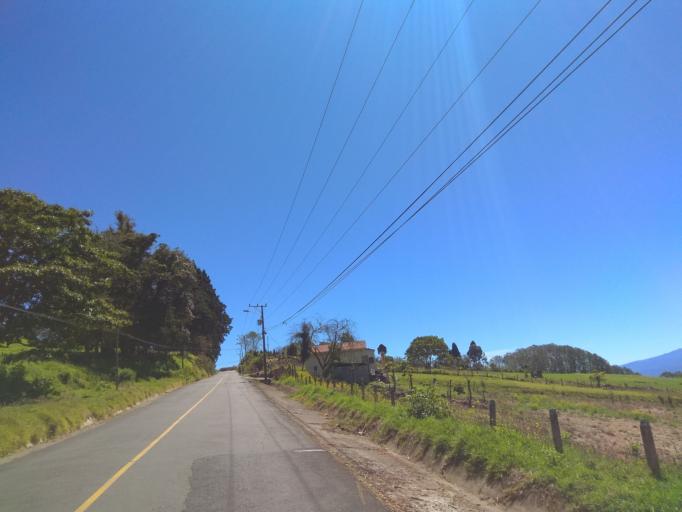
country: CR
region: Cartago
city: Tres Rios
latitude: 9.9418
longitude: -83.9286
